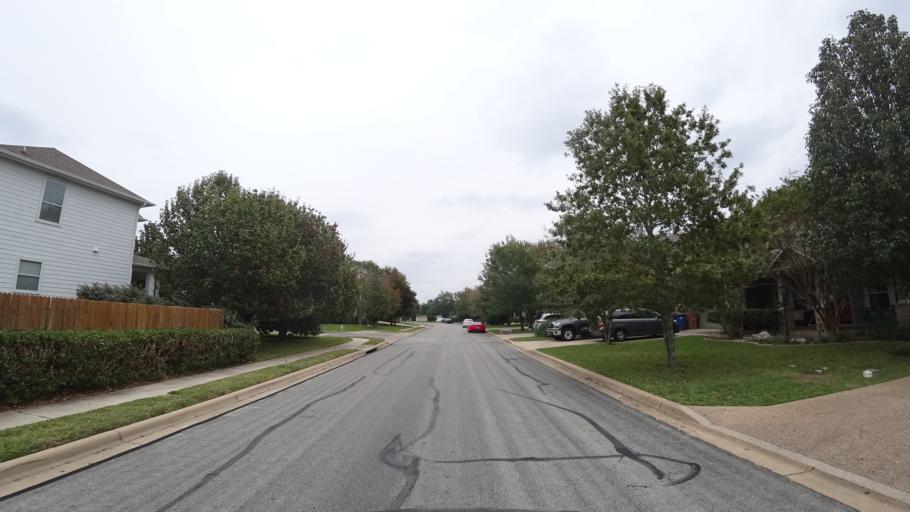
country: US
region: Texas
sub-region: Travis County
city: Shady Hollow
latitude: 30.2039
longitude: -97.8831
